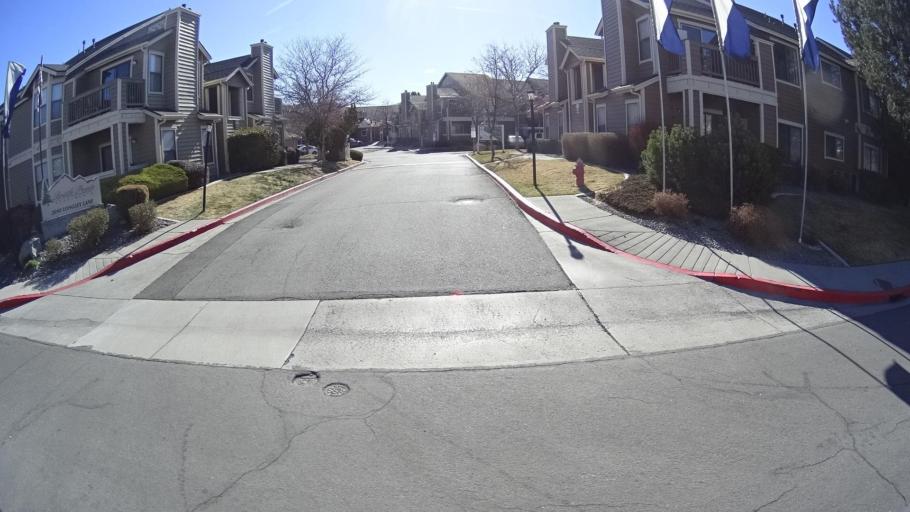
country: US
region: Nevada
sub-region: Washoe County
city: Sparks
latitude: 39.5011
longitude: -119.7504
